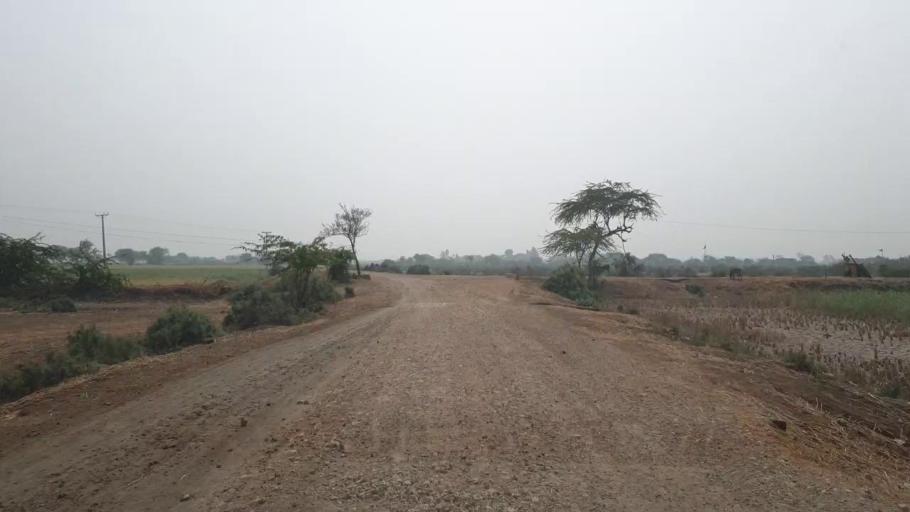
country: PK
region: Sindh
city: Kario
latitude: 24.6441
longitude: 68.6399
